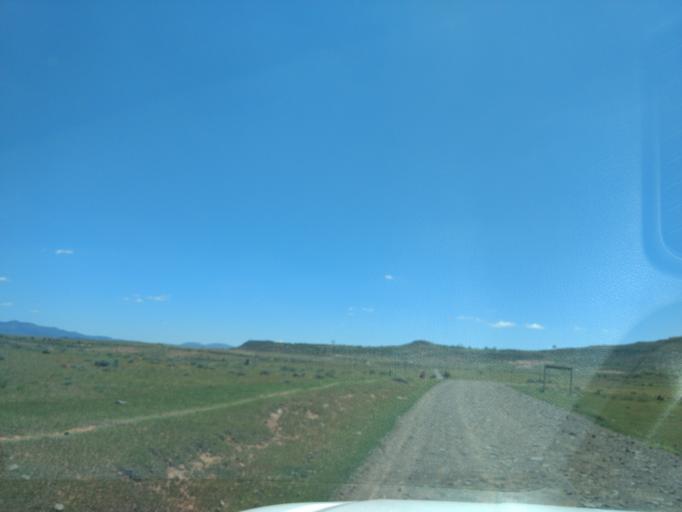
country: LS
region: Maseru
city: Maseru
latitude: -29.4759
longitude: 27.3749
